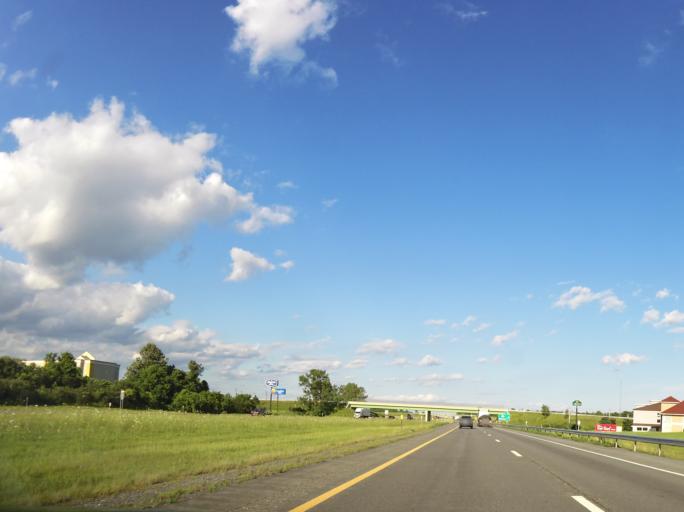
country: US
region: New York
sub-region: Genesee County
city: Batavia
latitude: 43.0180
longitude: -78.1958
